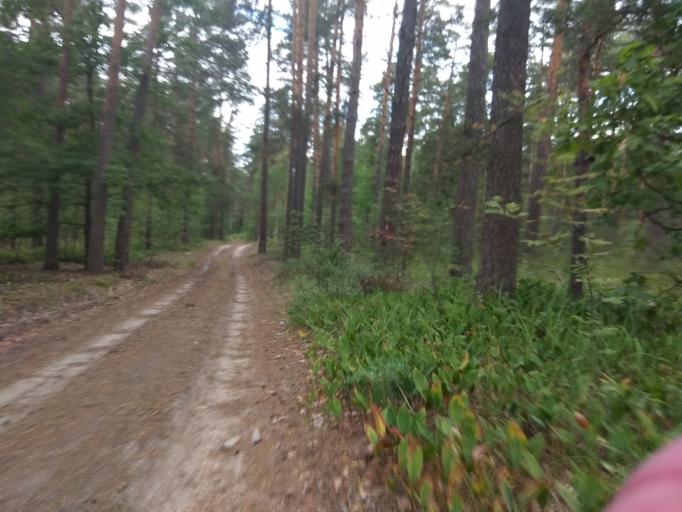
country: RU
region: Moskovskaya
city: Misheronskiy
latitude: 55.6372
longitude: 39.7285
